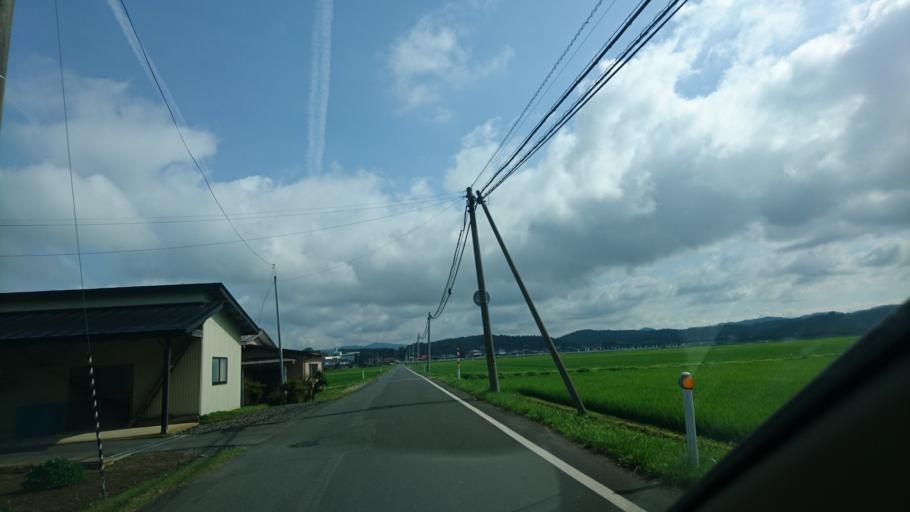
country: JP
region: Iwate
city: Mizusawa
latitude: 39.2049
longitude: 141.1513
